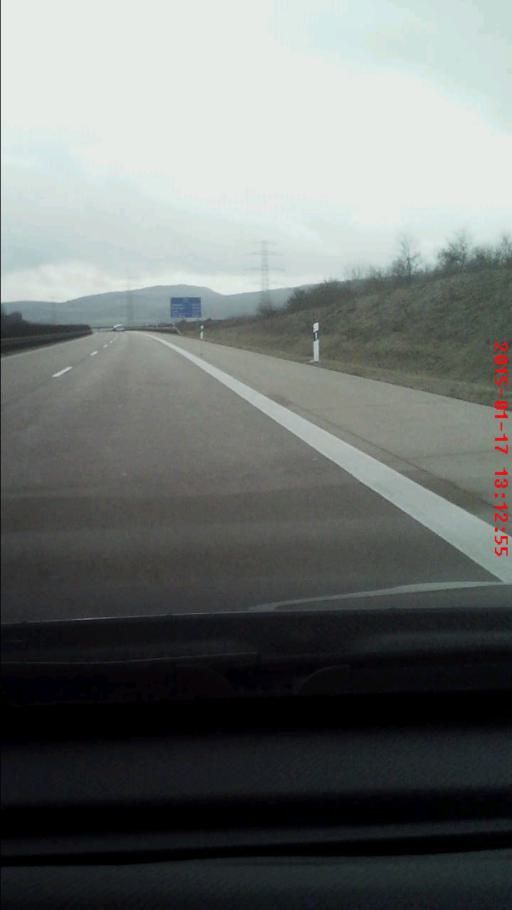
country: DE
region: Thuringia
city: Dornheim
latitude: 50.8173
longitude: 11.0016
